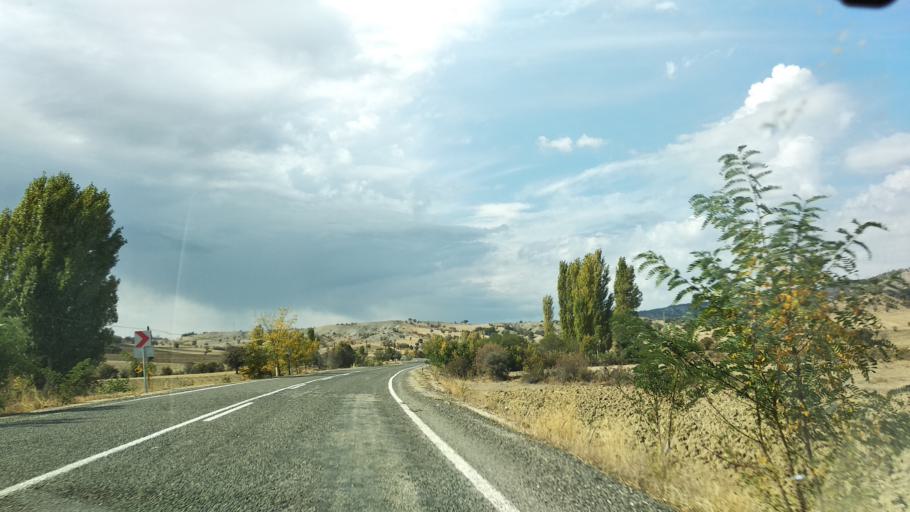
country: TR
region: Bolu
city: Seben
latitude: 40.3840
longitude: 31.5331
